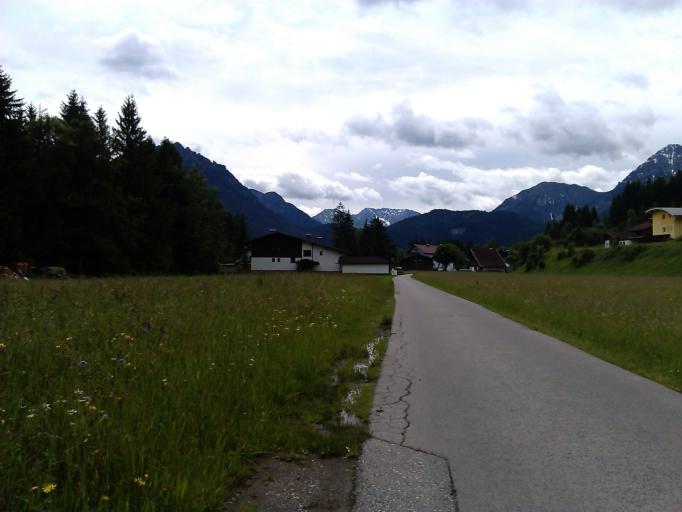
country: AT
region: Tyrol
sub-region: Politischer Bezirk Reutte
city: Lechaschau
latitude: 47.5017
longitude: 10.7053
